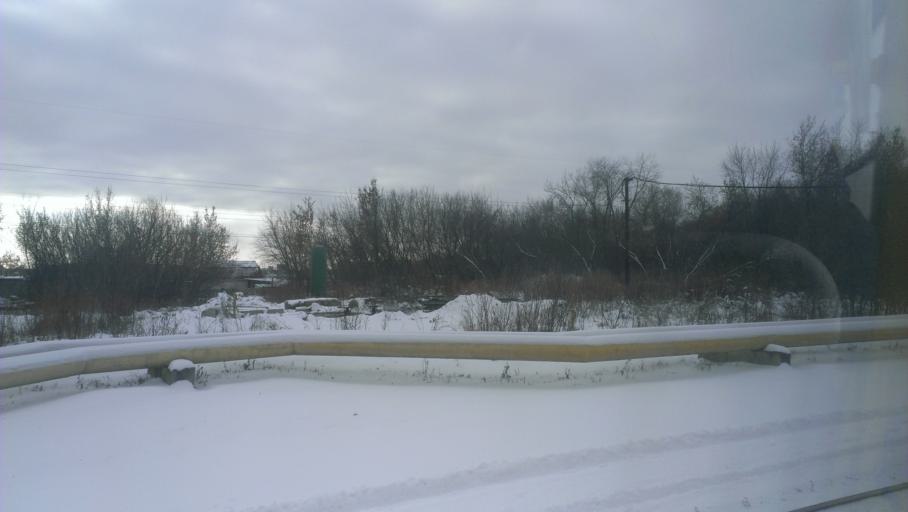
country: RU
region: Altai Krai
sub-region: Gorod Barnaulskiy
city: Barnaul
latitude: 53.3872
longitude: 83.7038
